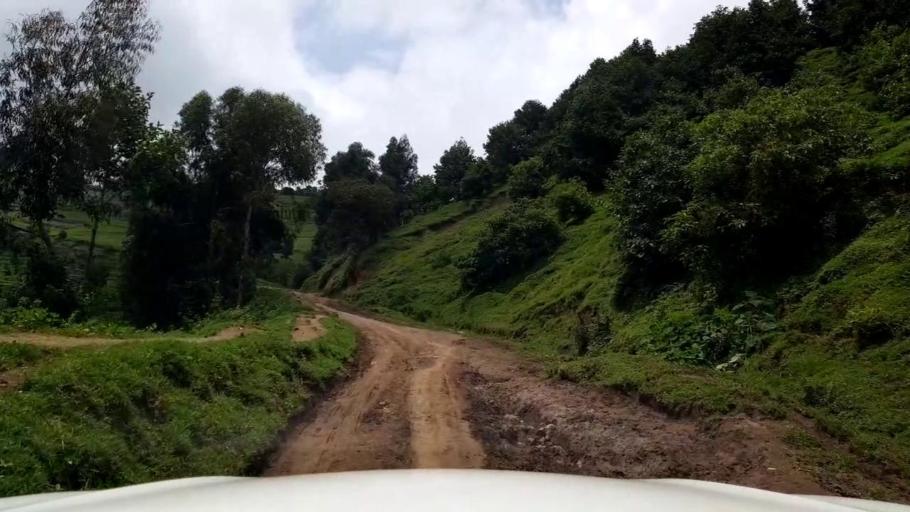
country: RW
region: Western Province
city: Gisenyi
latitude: -1.6674
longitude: 29.4126
